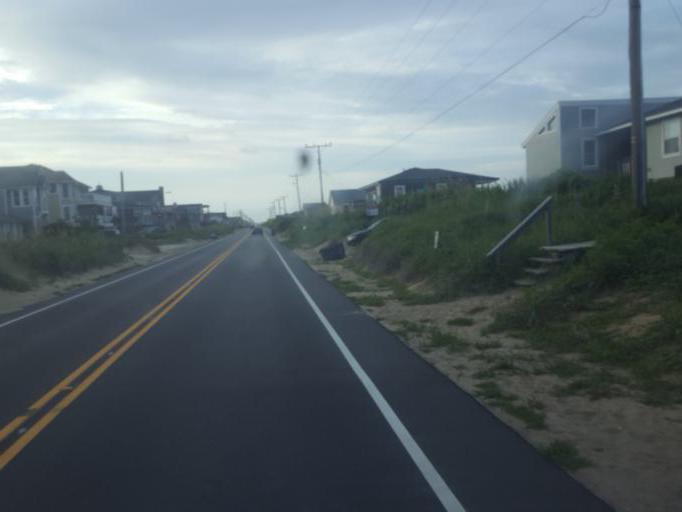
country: US
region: North Carolina
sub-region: Dare County
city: Kitty Hawk
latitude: 36.0597
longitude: -75.6857
